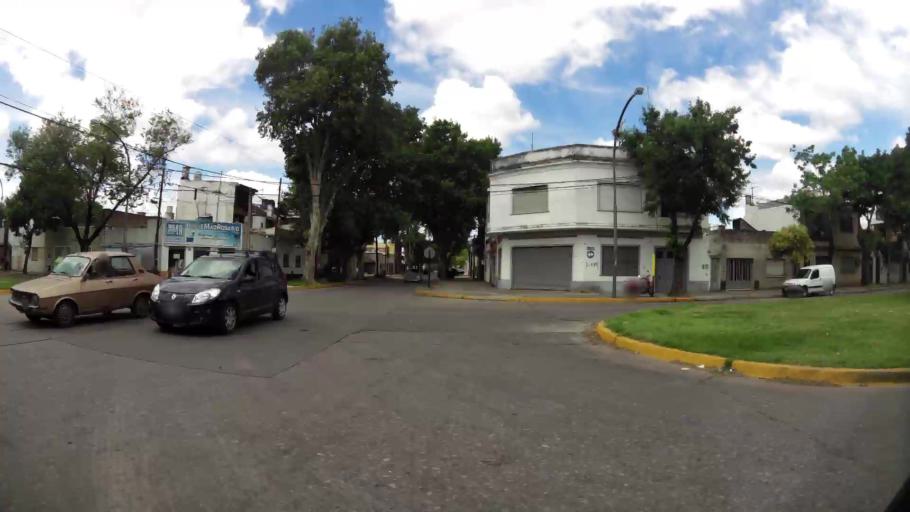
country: AR
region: Santa Fe
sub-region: Departamento de Rosario
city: Rosario
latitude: -32.9800
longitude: -60.6411
